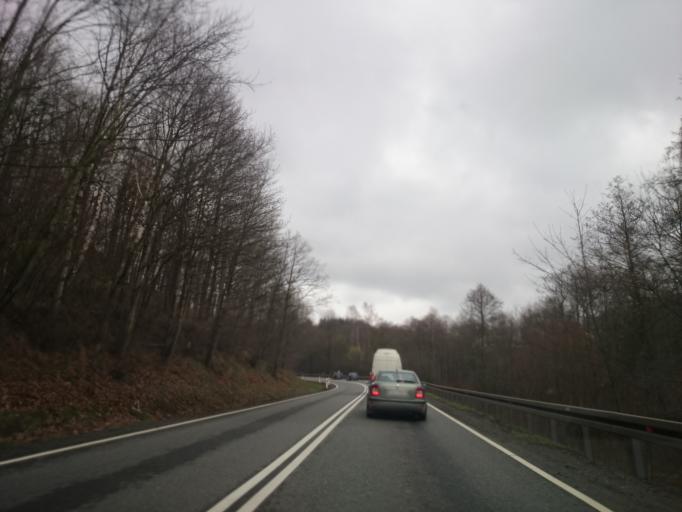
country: PL
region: Lower Silesian Voivodeship
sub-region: Powiat zabkowicki
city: Zloty Stok
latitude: 50.4364
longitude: 16.7984
